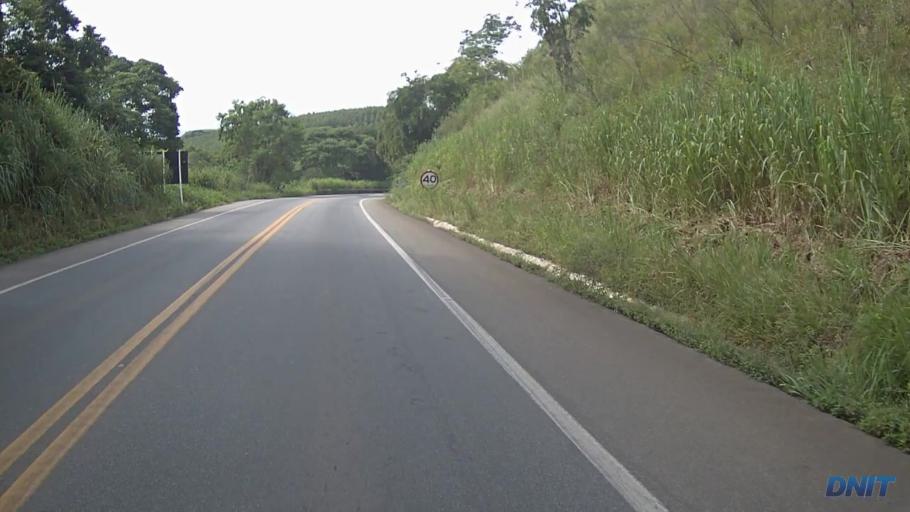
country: BR
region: Minas Gerais
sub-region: Ipaba
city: Ipaba
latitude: -19.3571
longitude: -42.4364
